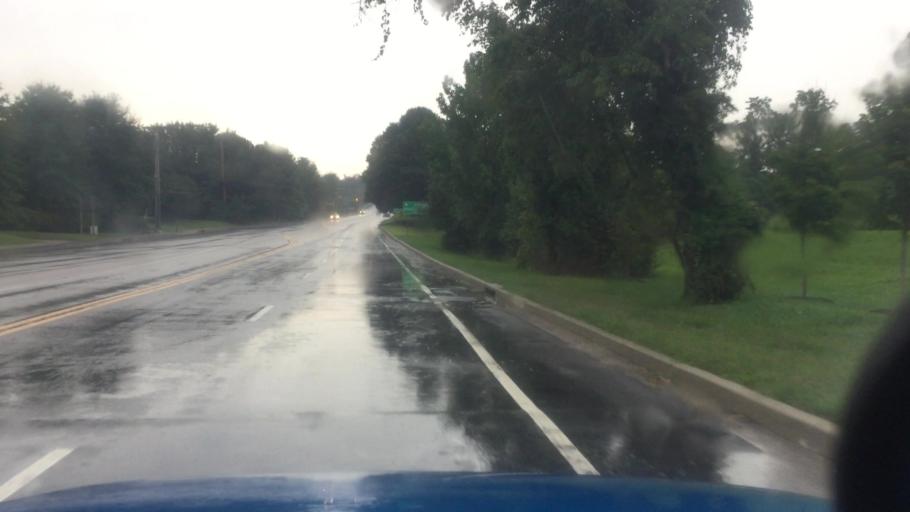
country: US
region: Maryland
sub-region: Howard County
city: Columbia
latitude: 39.2112
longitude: -76.8003
